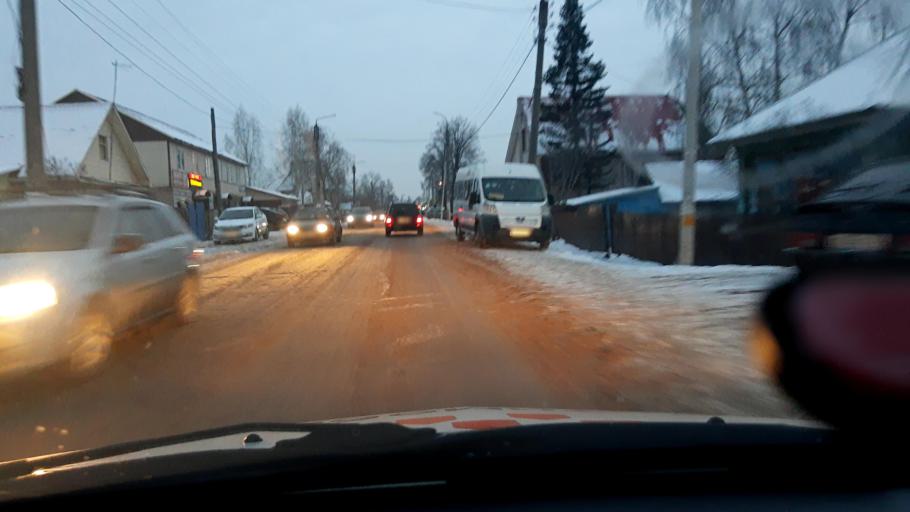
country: RU
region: Bashkortostan
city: Iglino
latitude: 54.8307
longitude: 56.4056
